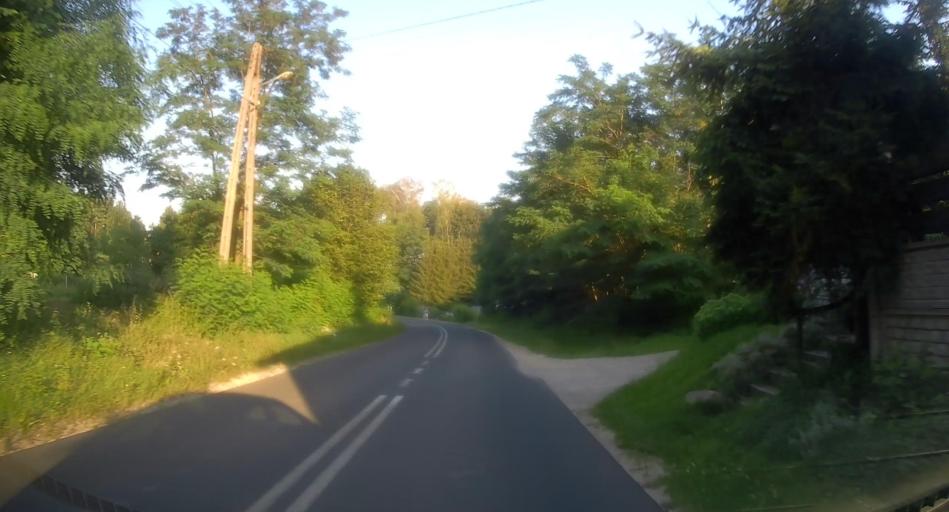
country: PL
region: Lodz Voivodeship
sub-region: Powiat skierniewicki
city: Kowiesy
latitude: 51.8971
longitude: 20.3765
